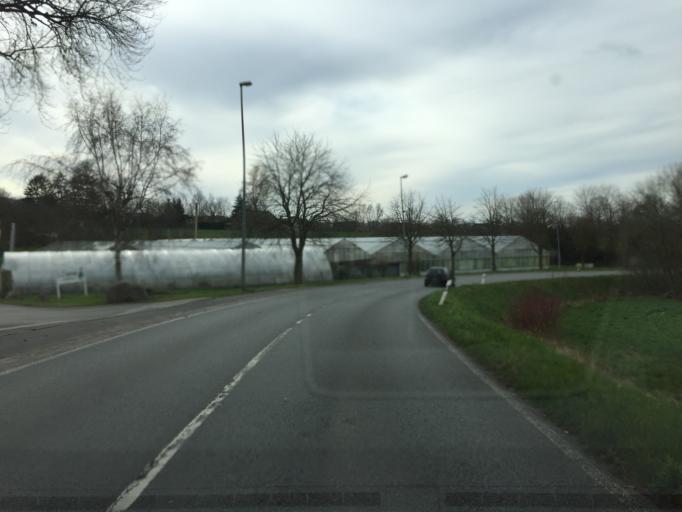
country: DE
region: North Rhine-Westphalia
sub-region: Regierungsbezirk Detmold
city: Bad Salzuflen
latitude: 52.0951
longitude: 8.7656
